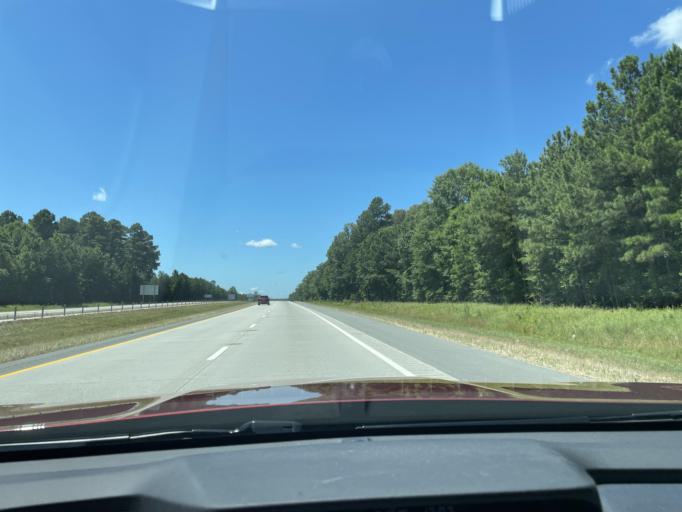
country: US
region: Arkansas
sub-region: Jefferson County
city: Pine Bluff
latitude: 34.1920
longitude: -91.9789
